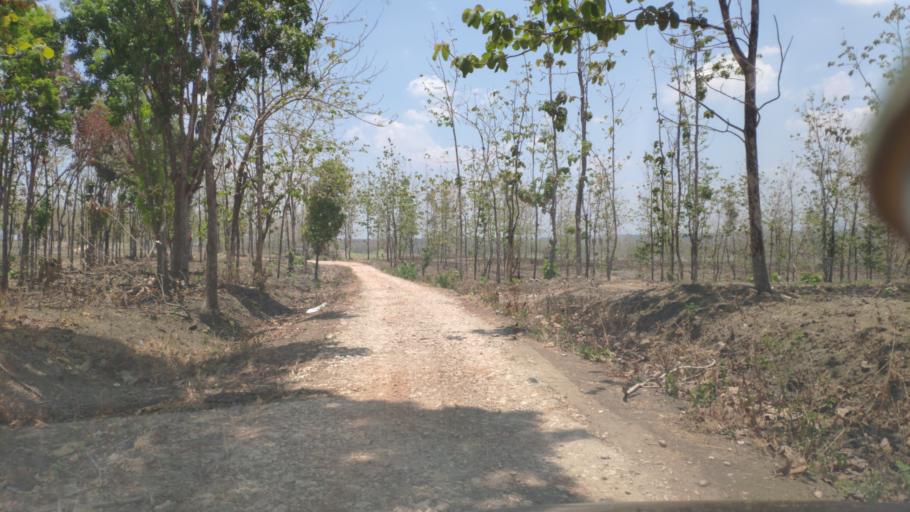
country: ID
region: West Java
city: Ngawi
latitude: -7.3259
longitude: 111.3598
